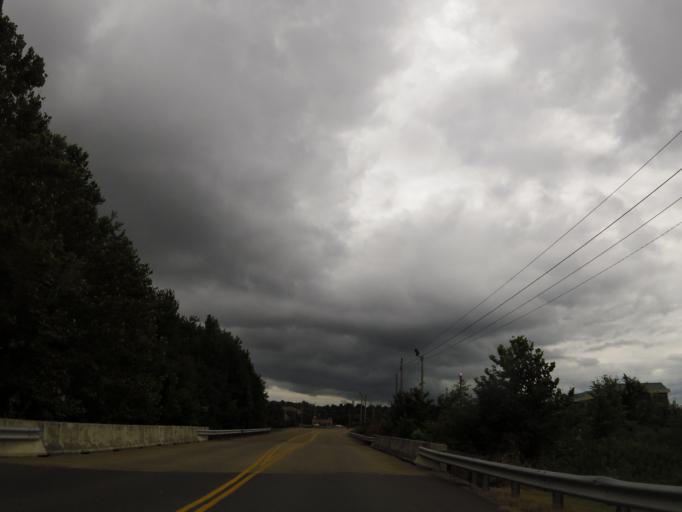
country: US
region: Kentucky
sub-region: McCracken County
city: Hendron
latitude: 37.0820
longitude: -88.6791
